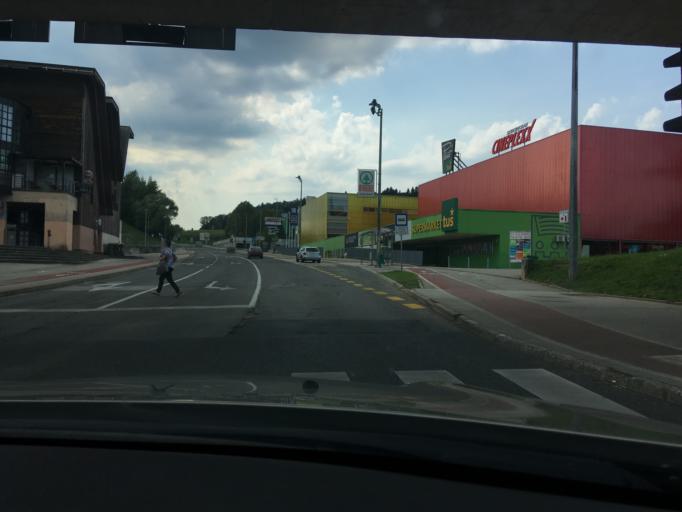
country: SI
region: Novo Mesto
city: Novo Mesto
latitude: 45.8022
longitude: 15.1616
